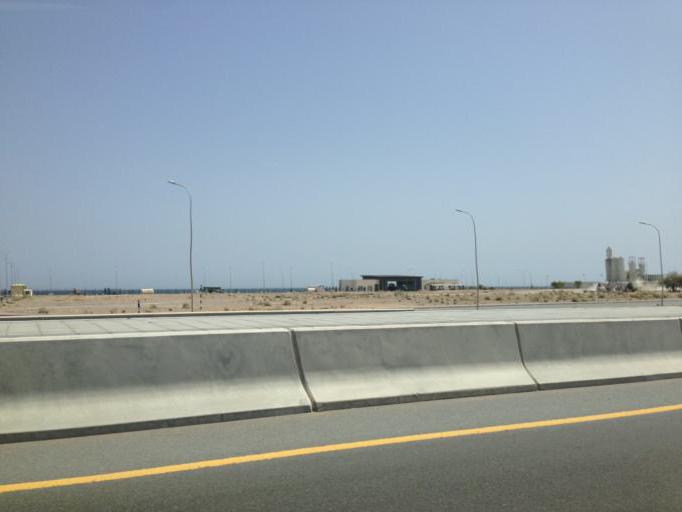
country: OM
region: Muhafazat Masqat
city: Bawshar
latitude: 23.6061
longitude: 58.3213
